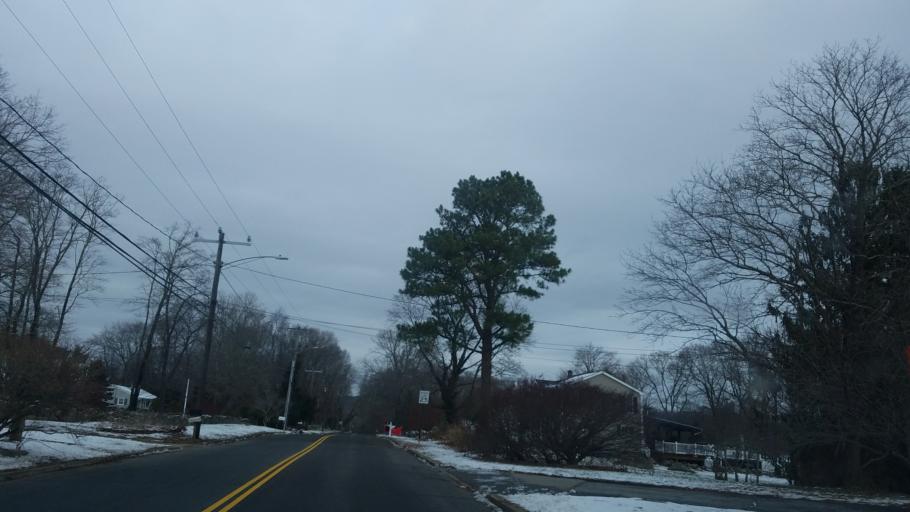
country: US
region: Connecticut
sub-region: New London County
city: Central Waterford
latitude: 41.3435
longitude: -72.1550
